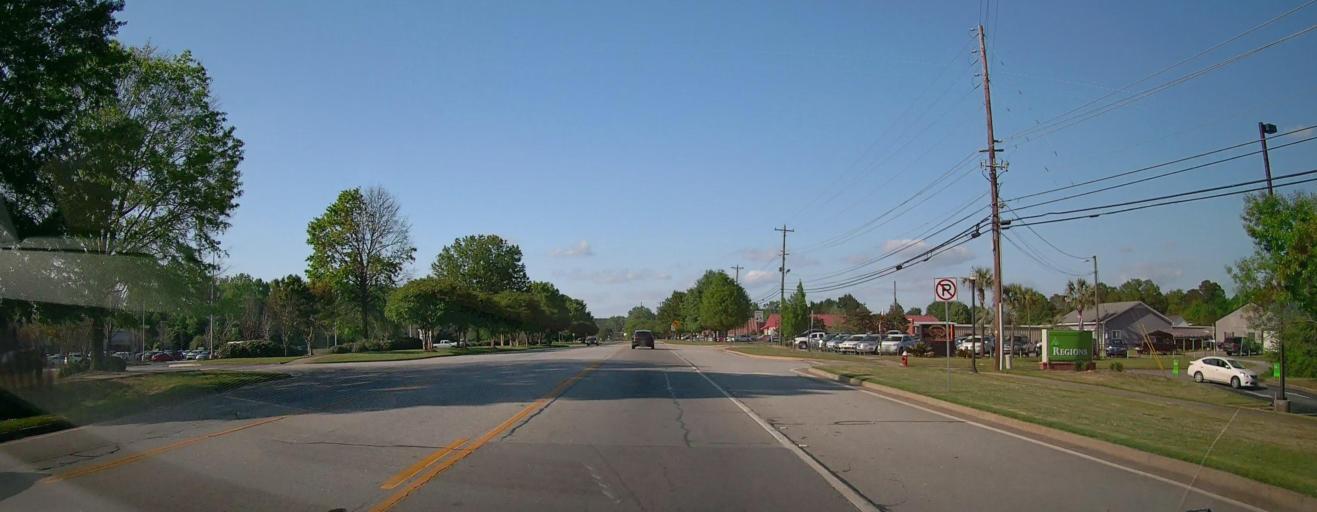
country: US
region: Georgia
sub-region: Morgan County
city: Madison
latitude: 33.5726
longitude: -83.4773
